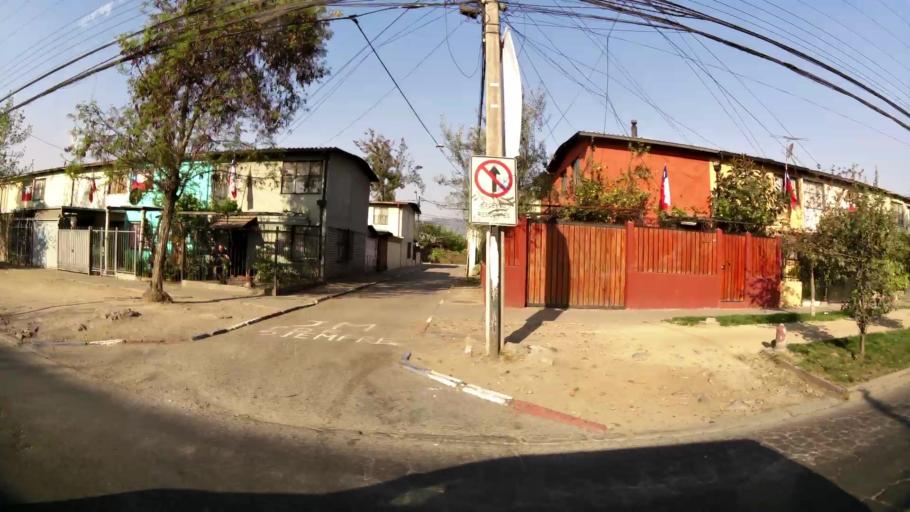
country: CL
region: Santiago Metropolitan
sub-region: Provincia de Santiago
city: Santiago
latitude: -33.4017
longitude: -70.6429
